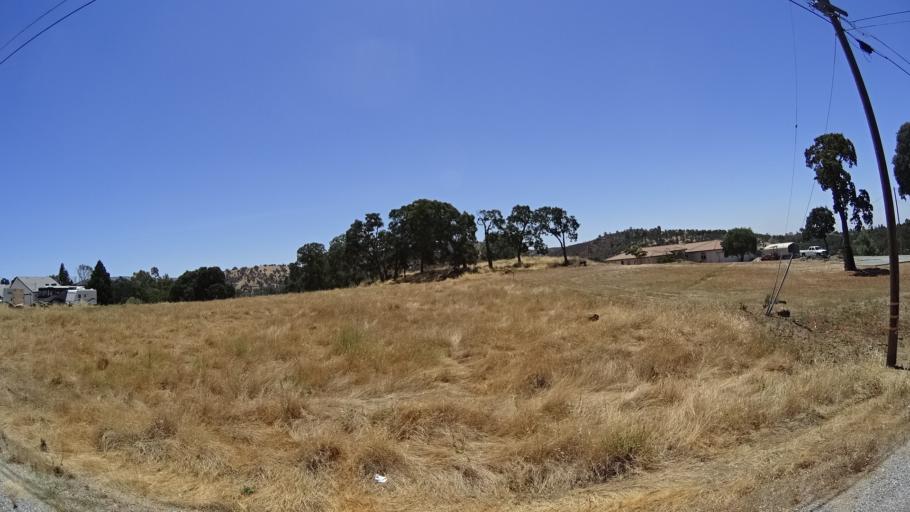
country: US
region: California
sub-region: Calaveras County
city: Rancho Calaveras
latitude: 38.1356
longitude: -120.8436
